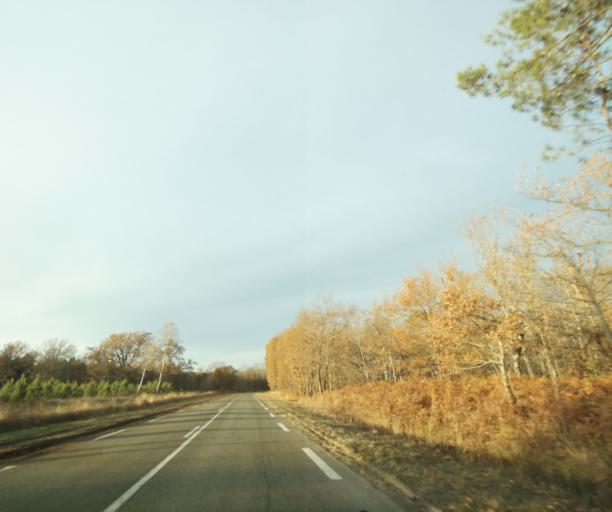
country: FR
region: Aquitaine
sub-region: Departement de la Gironde
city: Grignols
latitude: 44.1908
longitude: -0.1531
